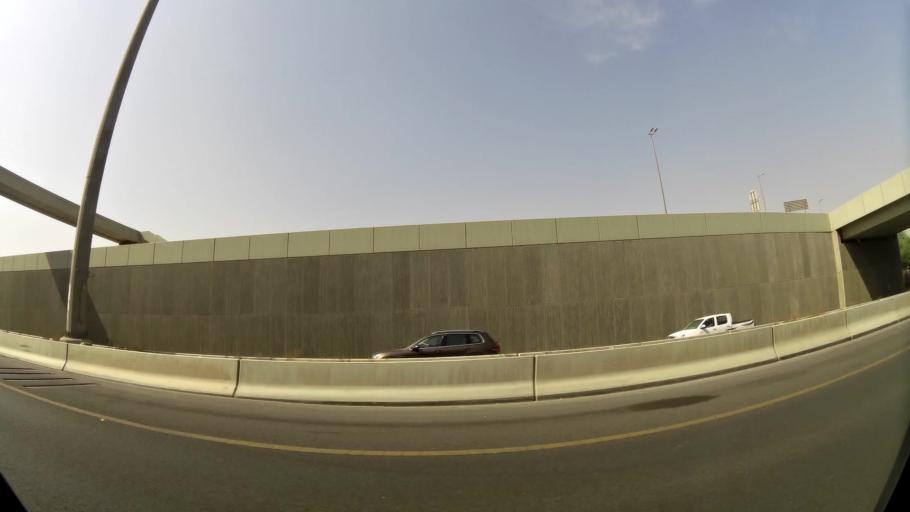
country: KW
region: Al Ahmadi
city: Al Manqaf
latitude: 29.1057
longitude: 48.1182
